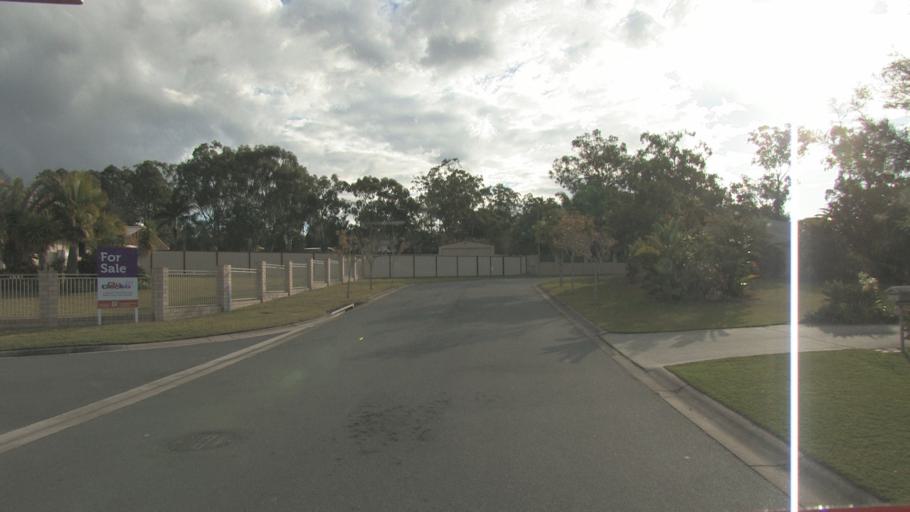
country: AU
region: Queensland
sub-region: Logan
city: Park Ridge South
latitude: -27.7062
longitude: 153.0225
